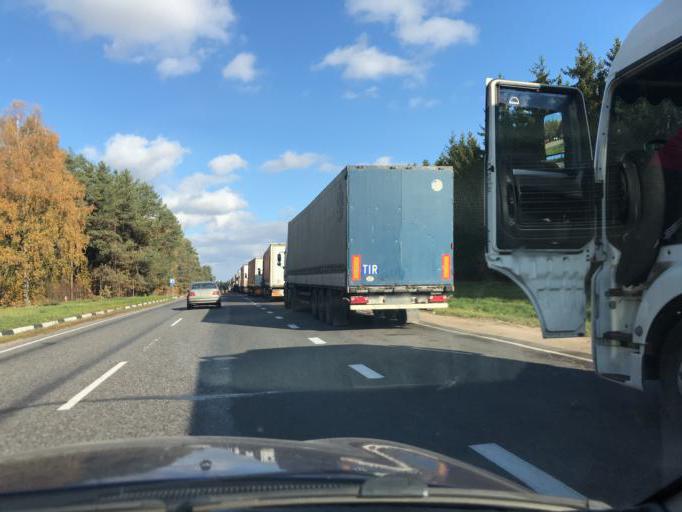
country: LT
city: Salcininkai
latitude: 54.2238
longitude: 25.3564
